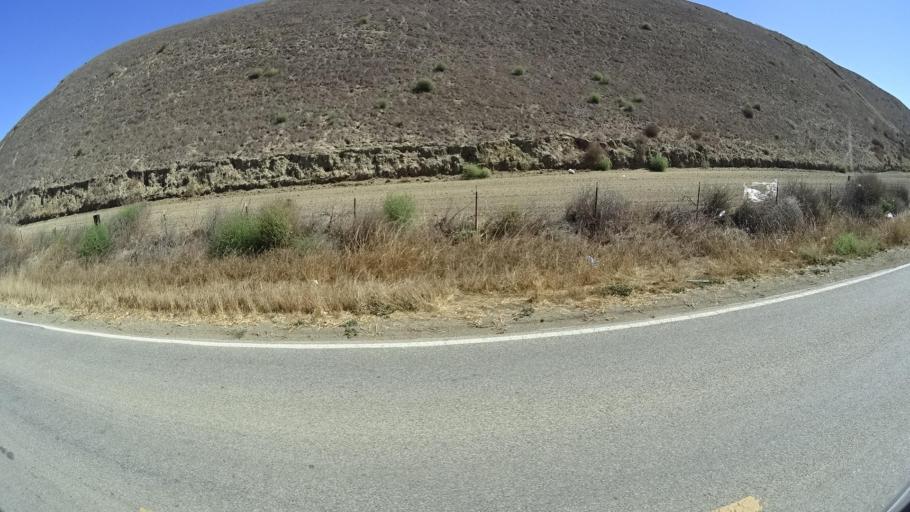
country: US
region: California
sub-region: Monterey County
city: King City
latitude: 36.2767
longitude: -121.1470
